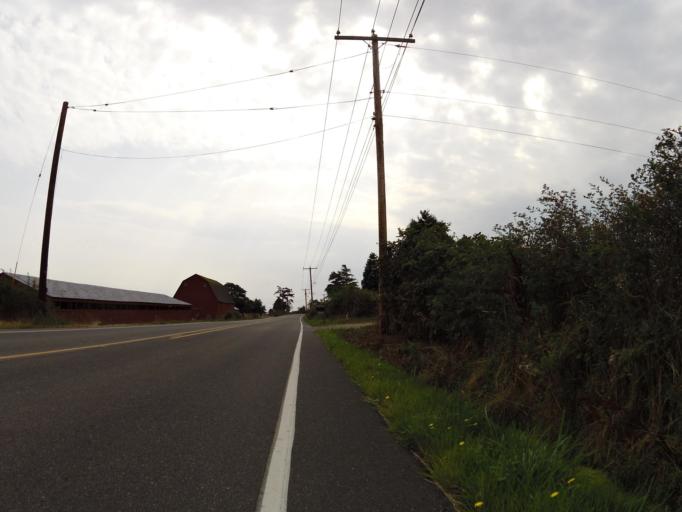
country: US
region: Washington
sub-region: Island County
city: Coupeville
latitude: 48.1907
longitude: -122.6681
